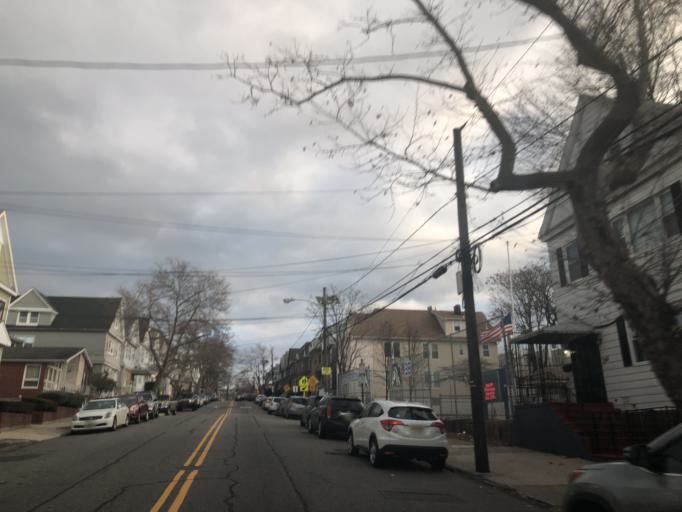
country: US
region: New Jersey
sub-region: Hudson County
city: Jersey City
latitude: 40.7095
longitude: -74.0909
